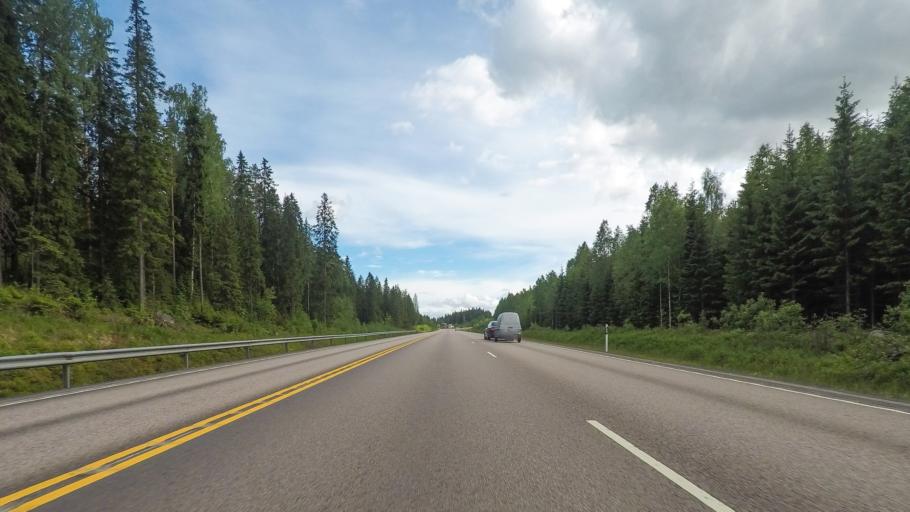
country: FI
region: Central Finland
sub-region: Jyvaeskylae
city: Toivakka
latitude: 62.0458
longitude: 26.0515
